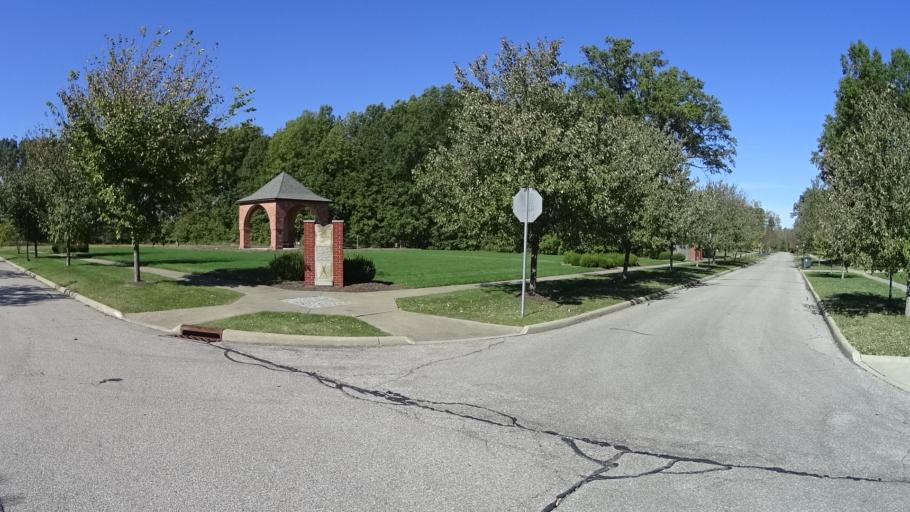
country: US
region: Ohio
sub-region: Lorain County
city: Oberlin
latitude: 41.2984
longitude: -82.2296
